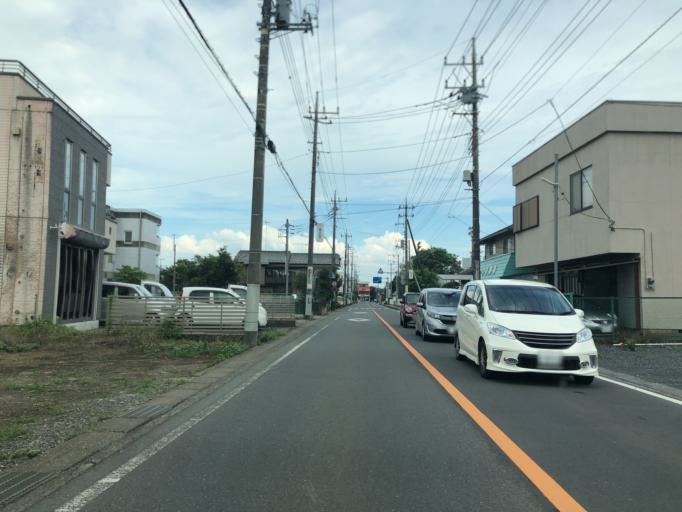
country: JP
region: Saitama
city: Fukiage-fujimi
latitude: 36.0434
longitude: 139.3976
